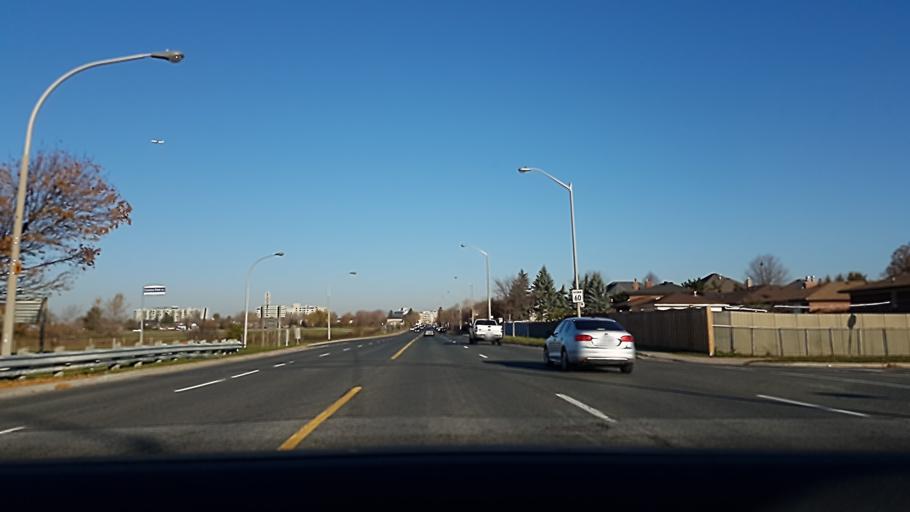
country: CA
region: Ontario
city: North York
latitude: 43.7428
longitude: -79.4524
